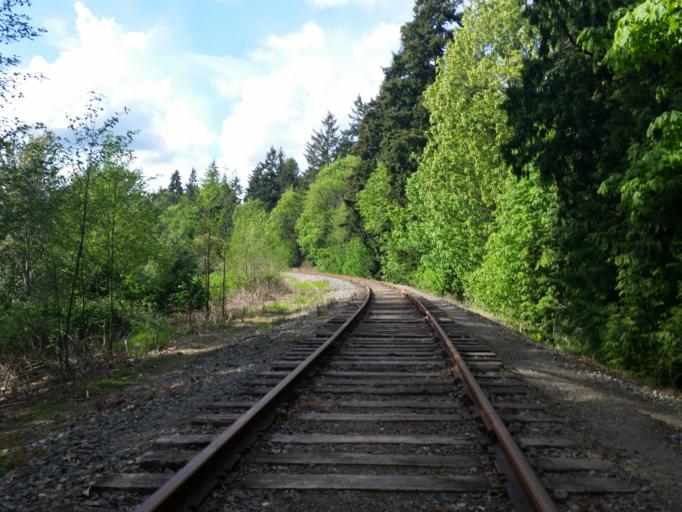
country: US
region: Washington
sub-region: King County
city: Yarrow Point
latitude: 47.6405
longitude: -122.1902
